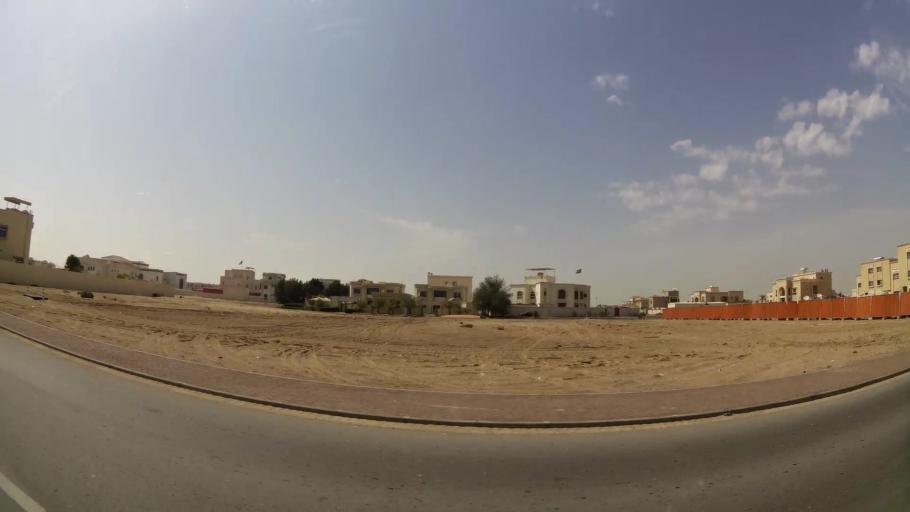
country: AE
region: Abu Dhabi
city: Abu Dhabi
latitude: 24.3148
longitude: 54.5748
